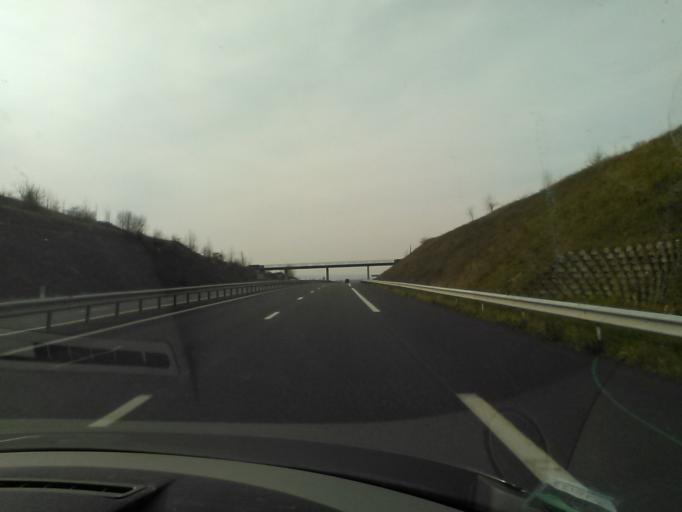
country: FR
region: Bourgogne
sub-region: Departement de l'Yonne
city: Soucy
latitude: 48.2607
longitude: 3.3180
